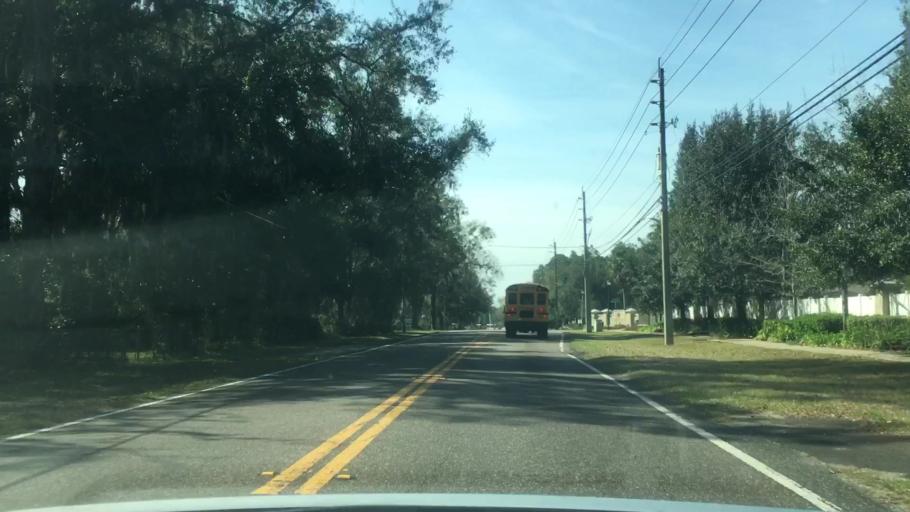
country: US
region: Florida
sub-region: Duval County
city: Jacksonville
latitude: 30.4621
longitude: -81.5743
